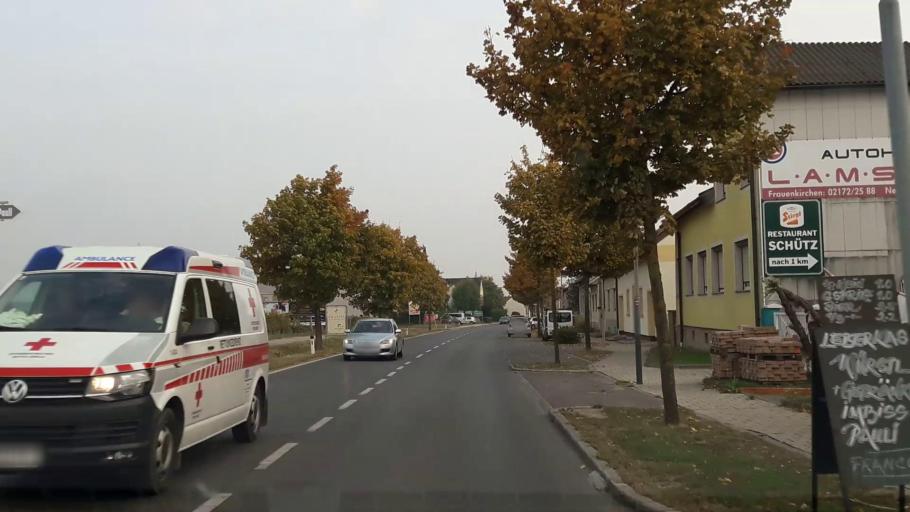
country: AT
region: Burgenland
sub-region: Politischer Bezirk Neusiedl am See
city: Weiden am See
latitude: 47.9335
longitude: 16.8606
